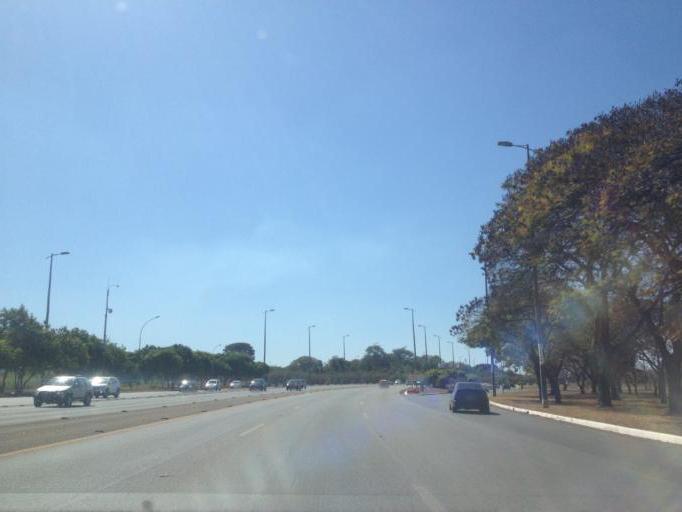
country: BR
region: Federal District
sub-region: Brasilia
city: Brasilia
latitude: -15.8393
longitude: -47.9305
